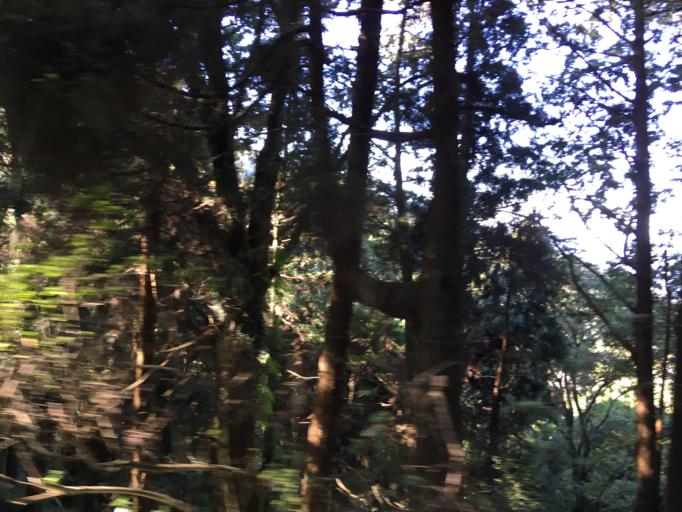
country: TW
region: Taiwan
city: Lugu
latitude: 23.5178
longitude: 120.8057
